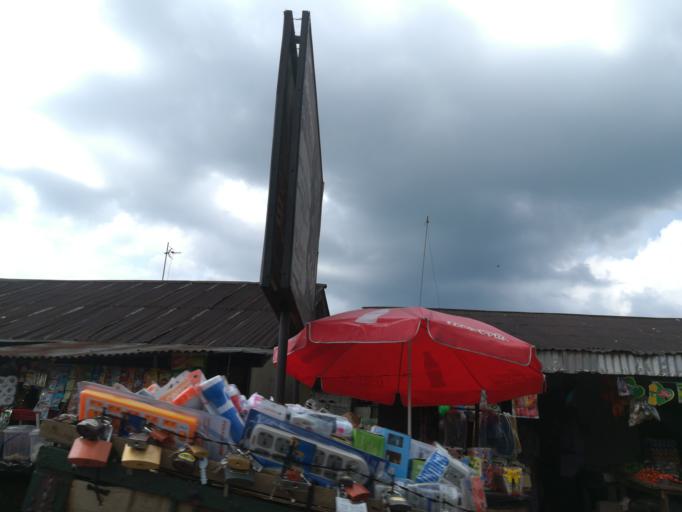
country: NG
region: Rivers
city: Okrika
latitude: 4.7298
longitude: 7.1470
